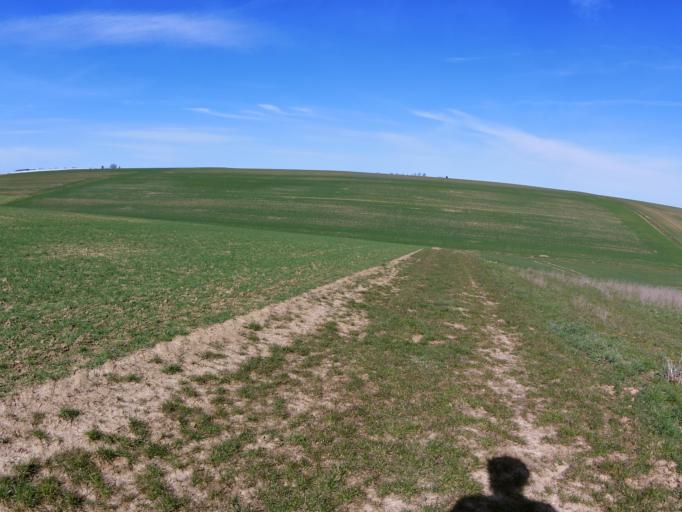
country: DE
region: Bavaria
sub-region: Regierungsbezirk Unterfranken
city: Biebelried
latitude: 49.7904
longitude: 10.0963
